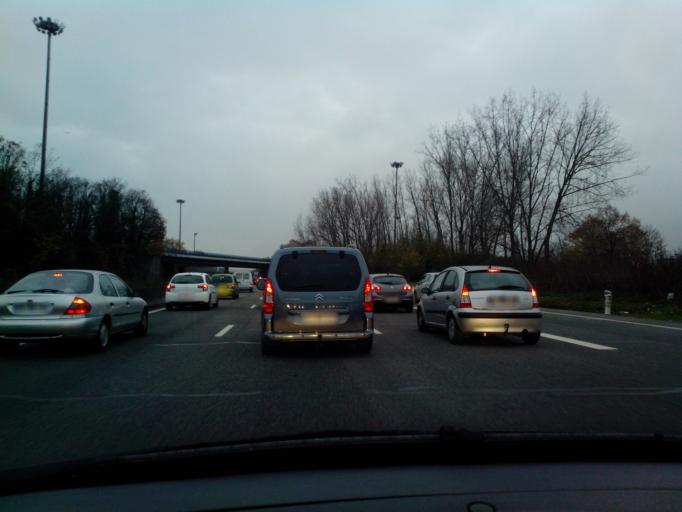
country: FR
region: Ile-de-France
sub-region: Departement de l'Essonne
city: Wissous
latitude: 48.7376
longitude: 2.3175
